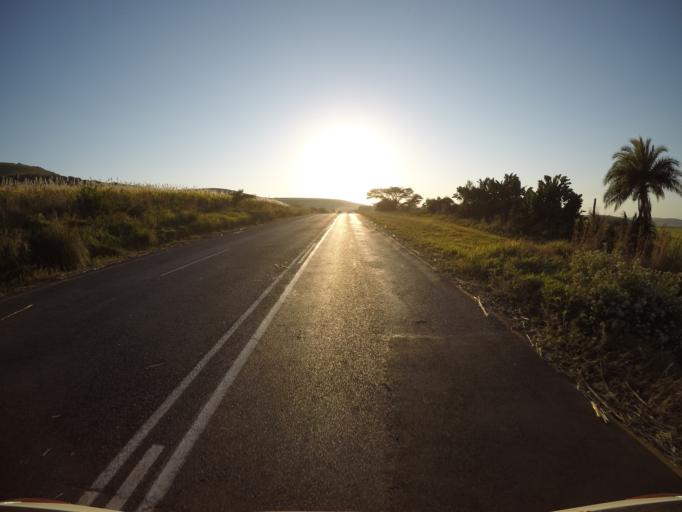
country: ZA
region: KwaZulu-Natal
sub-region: uThungulu District Municipality
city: Eshowe
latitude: -28.9514
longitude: 31.6702
